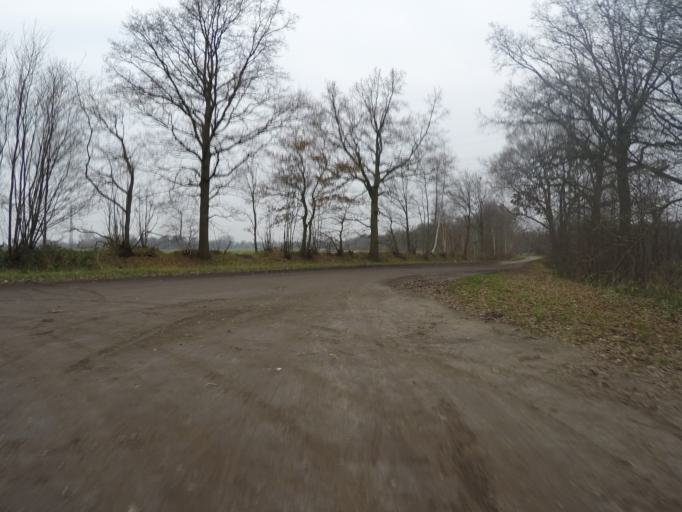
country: DE
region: Schleswig-Holstein
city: Borstel-Hohenraden
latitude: 53.6768
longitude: 9.8185
